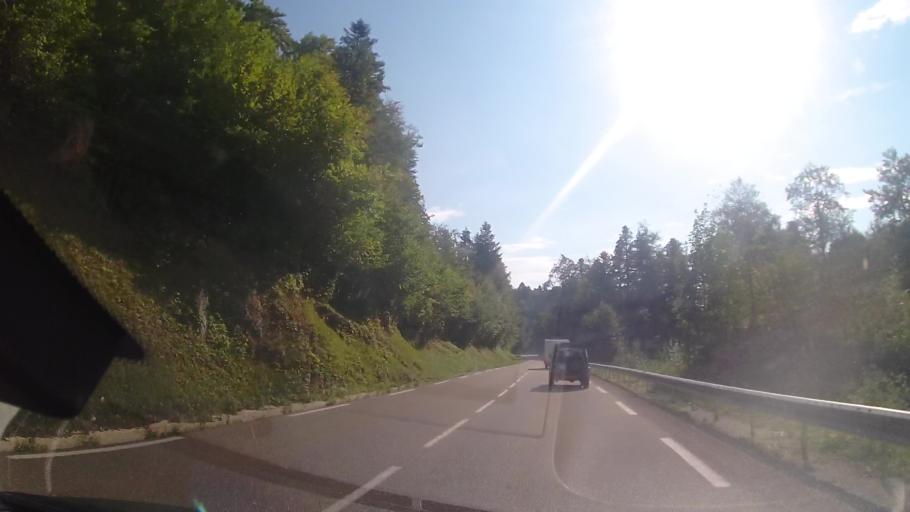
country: FR
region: Franche-Comte
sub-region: Departement du Jura
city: Champagnole
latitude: 46.6090
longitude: 5.8876
